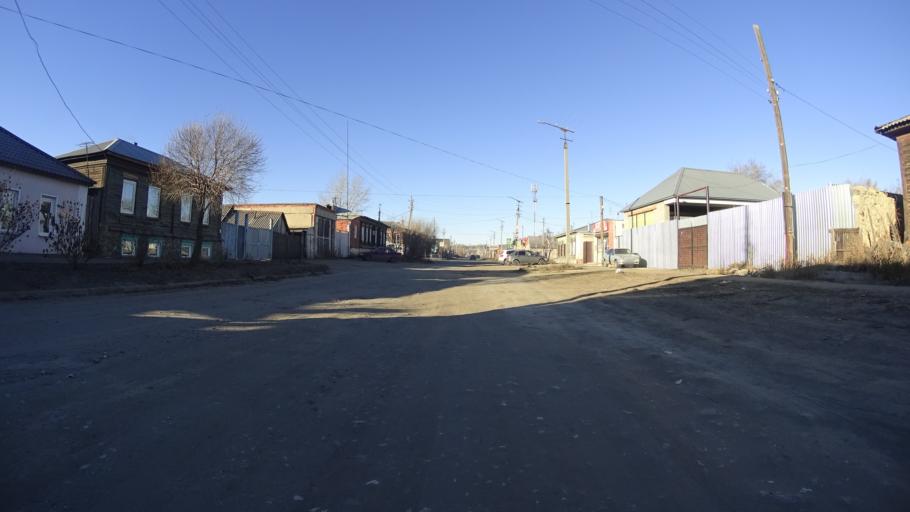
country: RU
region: Chelyabinsk
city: Troitsk
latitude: 54.0848
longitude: 61.5674
